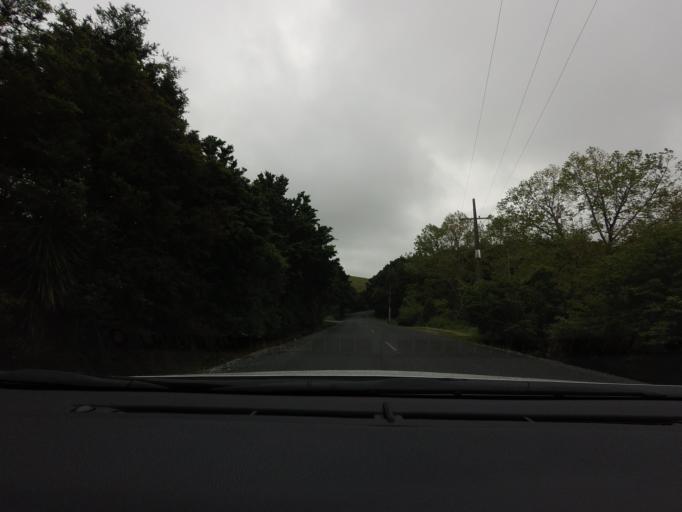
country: NZ
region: Auckland
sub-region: Auckland
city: Wellsford
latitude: -36.2787
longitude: 174.5865
